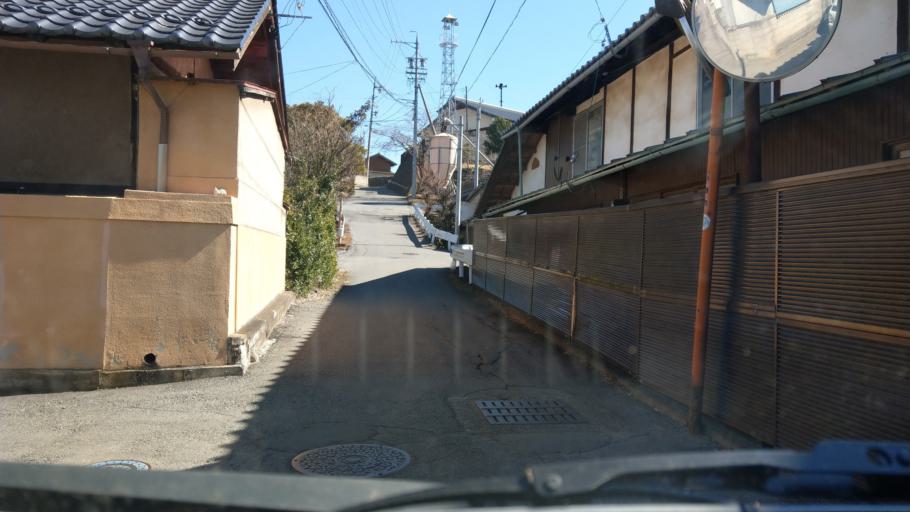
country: JP
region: Nagano
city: Komoro
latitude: 36.3307
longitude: 138.4017
